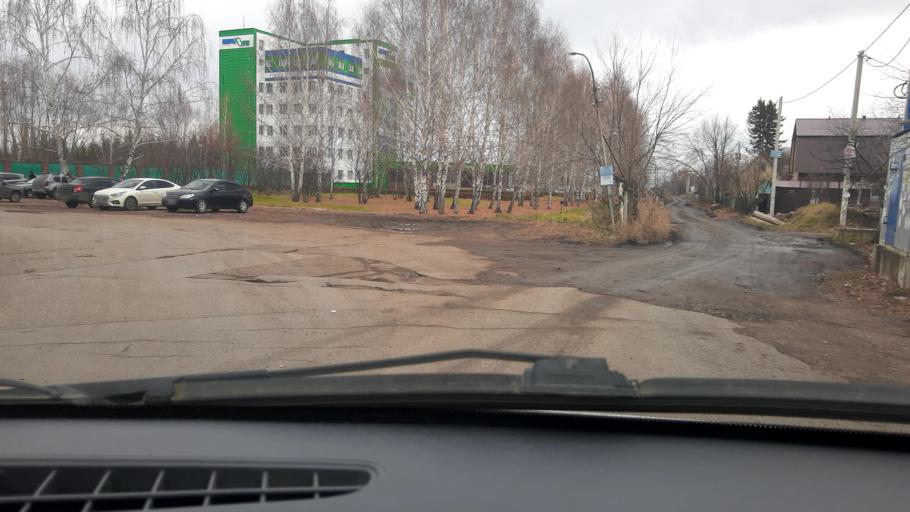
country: RU
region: Bashkortostan
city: Avdon
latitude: 54.7149
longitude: 55.8102
